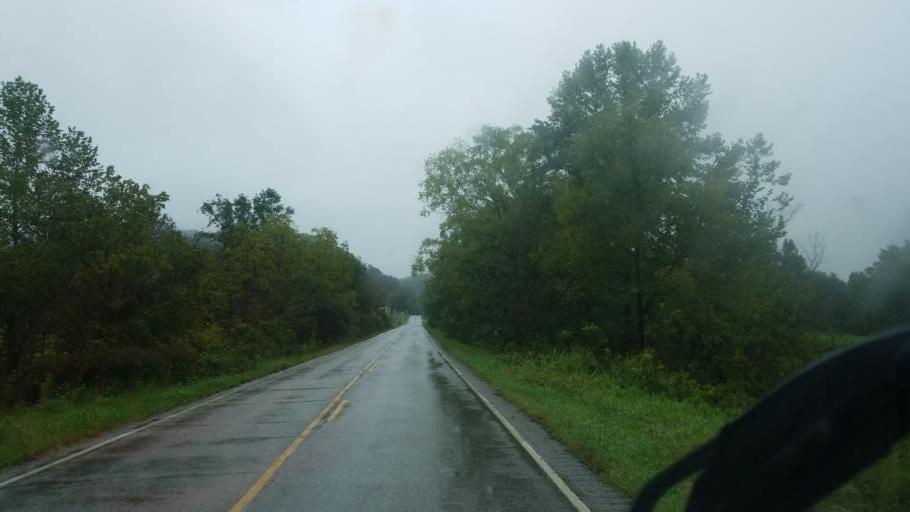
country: US
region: Kentucky
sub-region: Greenup County
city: South Shore
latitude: 38.7019
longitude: -82.9445
